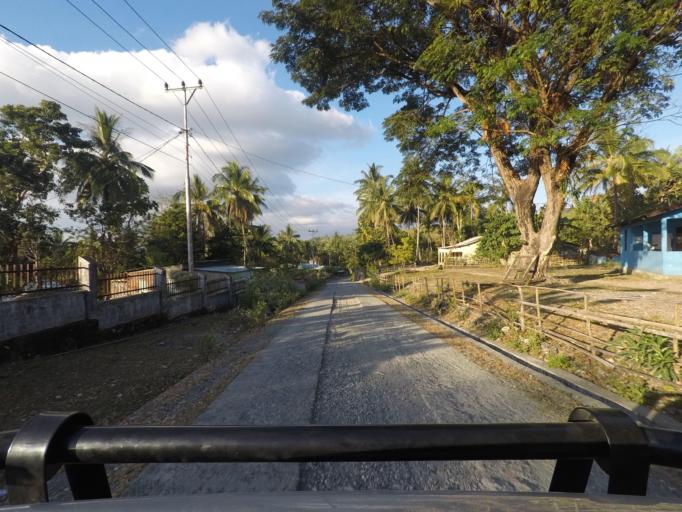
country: TL
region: Bobonaro
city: Maliana
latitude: -8.9686
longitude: 125.0457
